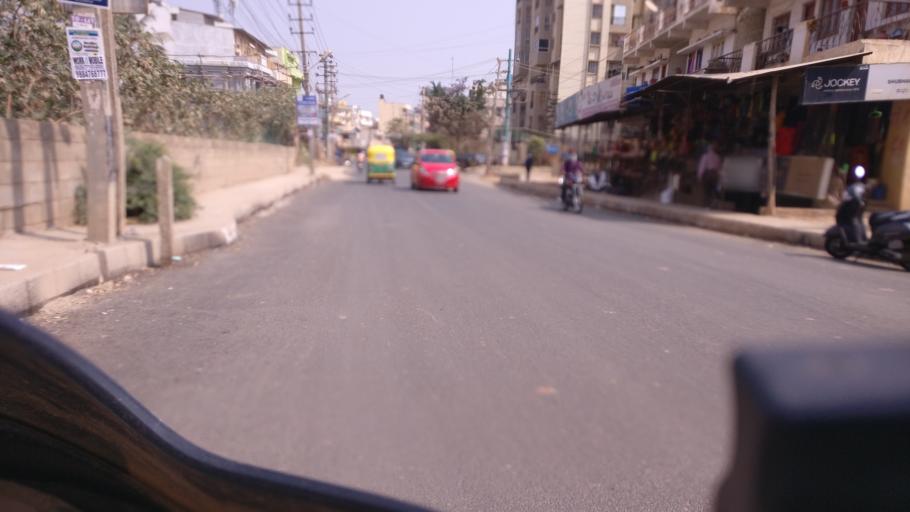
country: IN
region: Karnataka
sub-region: Bangalore Urban
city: Bangalore
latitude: 12.9061
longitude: 77.6757
